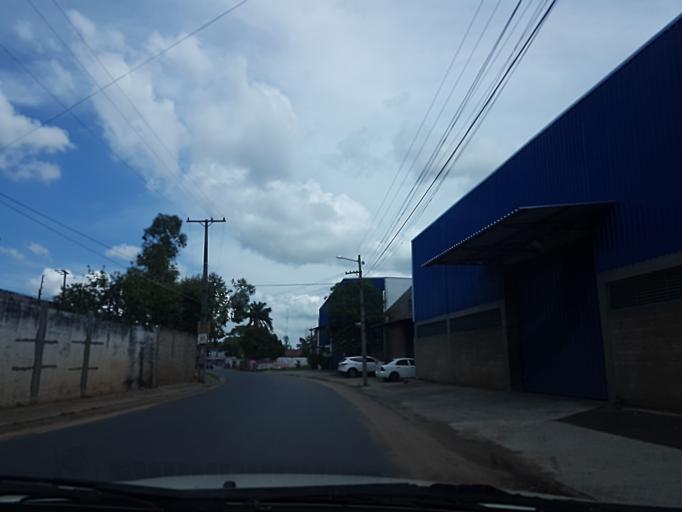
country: PY
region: Central
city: Colonia Mariano Roque Alonso
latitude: -25.2286
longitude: -57.5326
